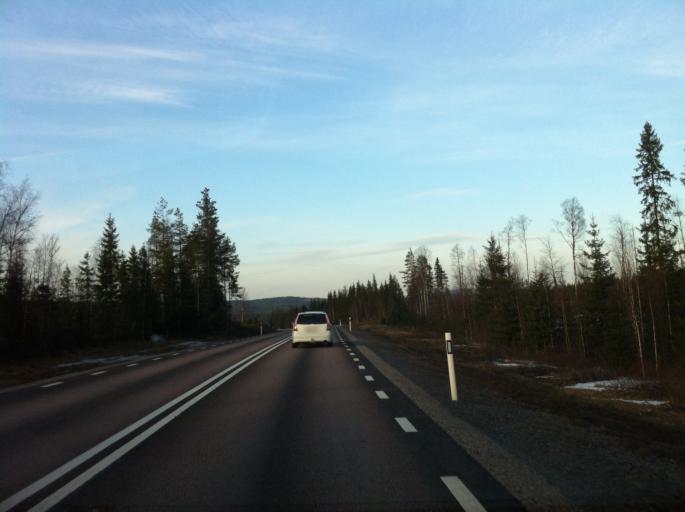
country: SE
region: Vaermland
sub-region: Filipstads Kommun
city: Lesjofors
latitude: 60.0714
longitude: 14.1379
